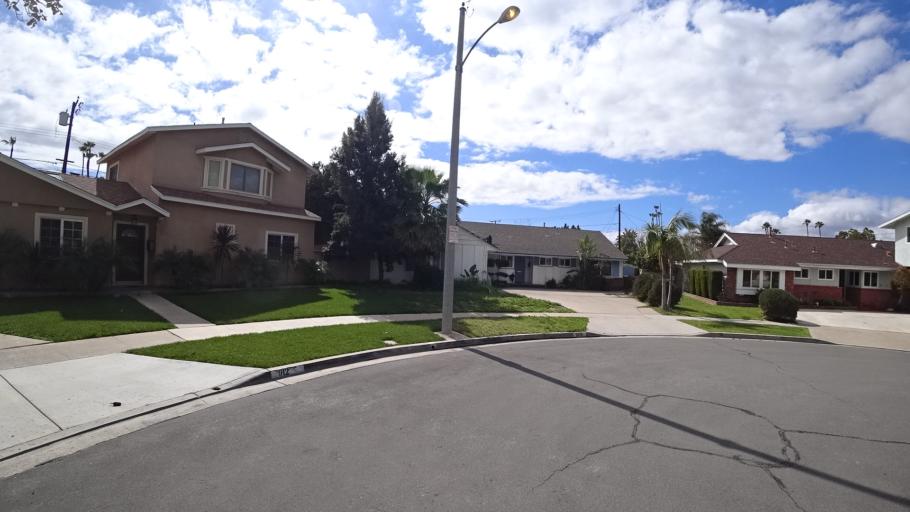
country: US
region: California
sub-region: Orange County
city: Anaheim
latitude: 33.8200
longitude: -117.9466
